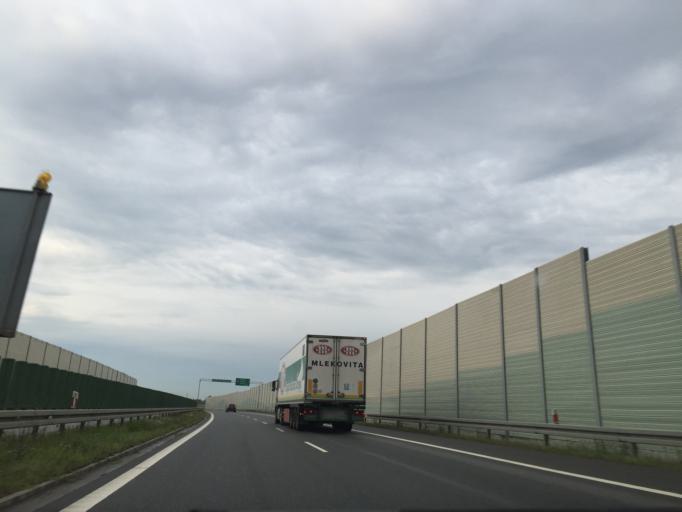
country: PL
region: Podlasie
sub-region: Powiat zambrowski
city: Zambrow
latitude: 52.9669
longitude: 22.2044
